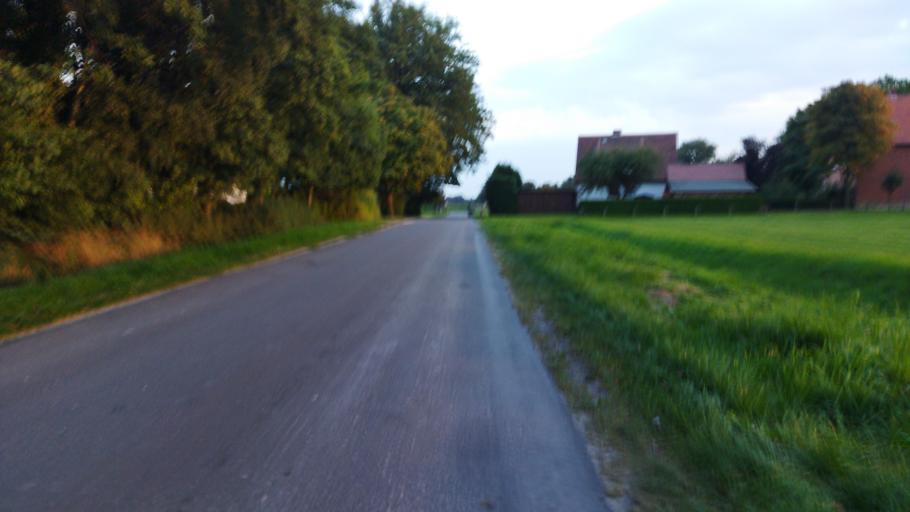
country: DE
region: Lower Saxony
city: Bad Iburg
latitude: 52.1308
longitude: 8.0565
